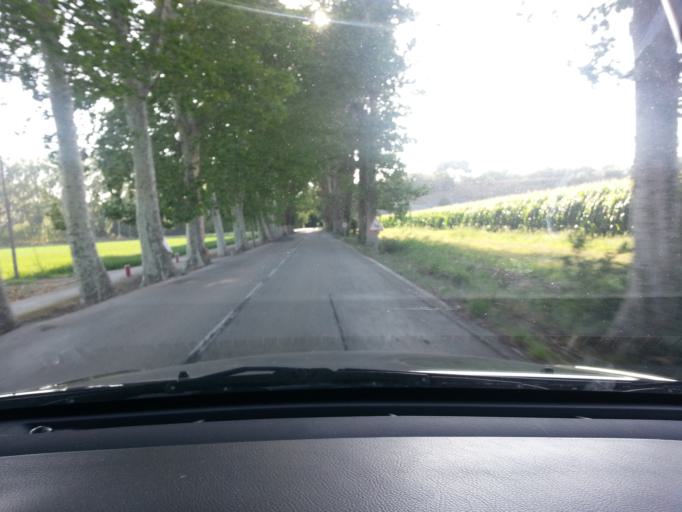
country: ES
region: Catalonia
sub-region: Provincia de Girona
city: Pals
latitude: 42.0128
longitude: 3.1698
